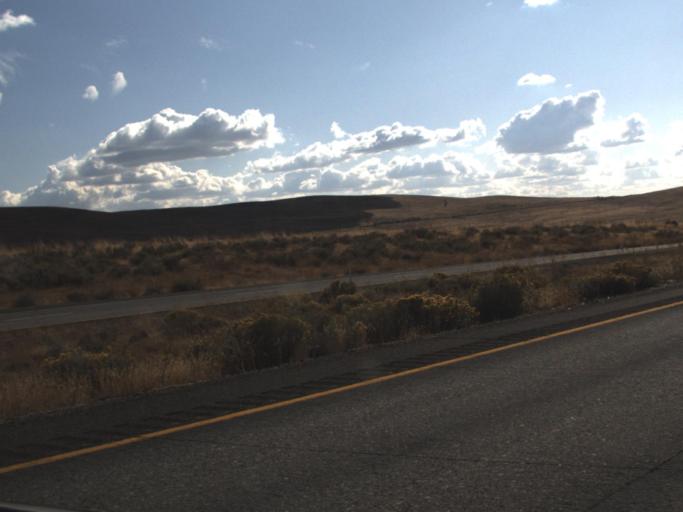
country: US
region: Oregon
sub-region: Umatilla County
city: Umatilla
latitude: 46.0106
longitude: -119.2353
